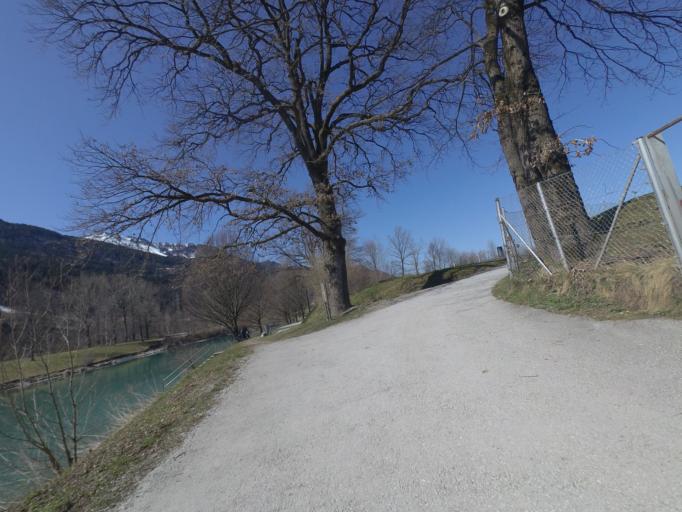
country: AT
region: Salzburg
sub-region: Politischer Bezirk Hallein
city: Kuchl
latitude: 47.6223
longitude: 13.1423
